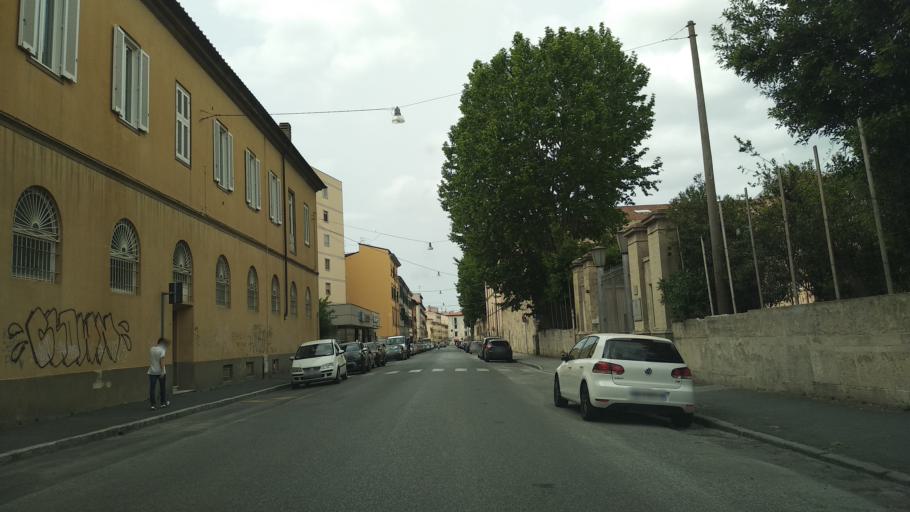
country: IT
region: Tuscany
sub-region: Provincia di Livorno
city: Livorno
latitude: 43.5539
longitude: 10.3190
